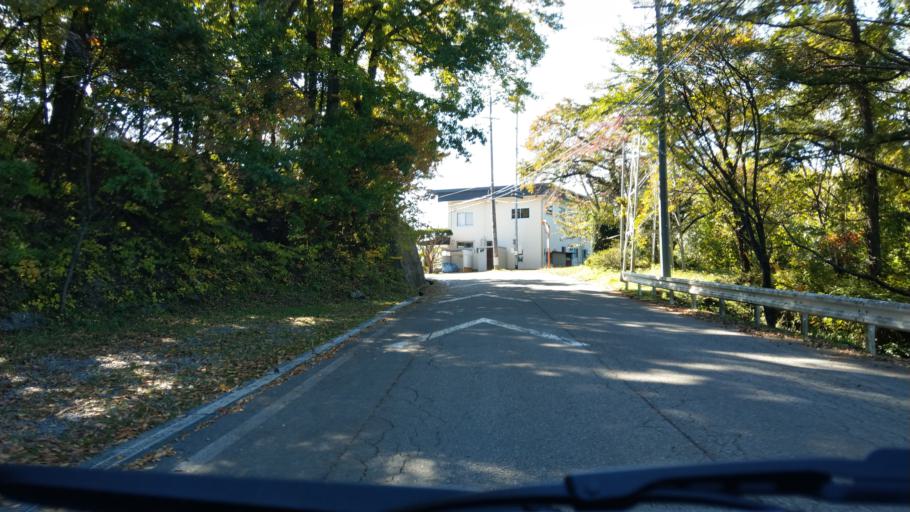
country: JP
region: Nagano
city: Komoro
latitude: 36.3631
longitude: 138.4010
